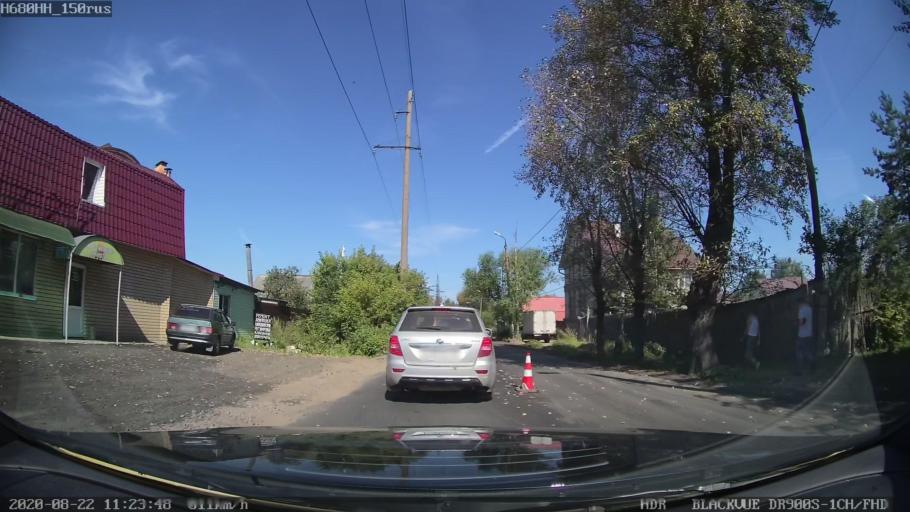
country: RU
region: Tverskaya
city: Tver
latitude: 56.8785
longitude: 35.9295
